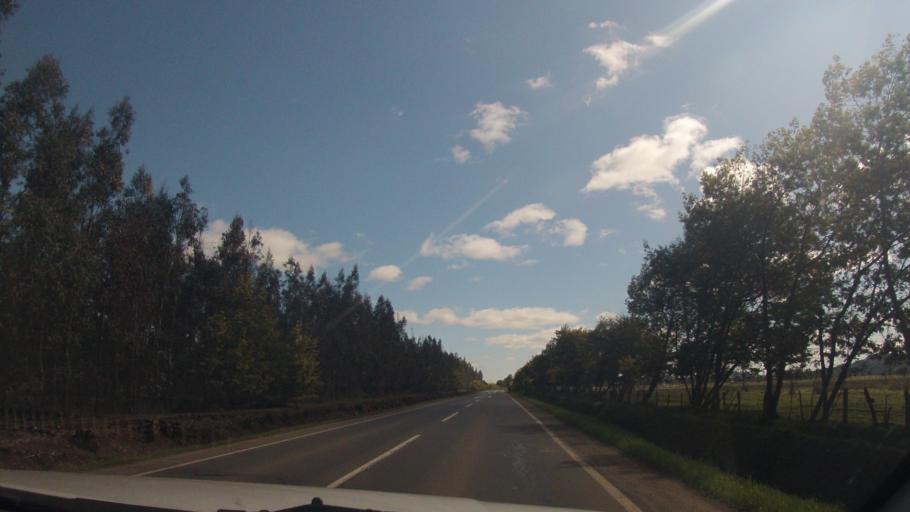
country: CL
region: Araucania
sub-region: Provincia de Malleco
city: Traiguen
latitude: -38.2623
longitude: -72.6106
